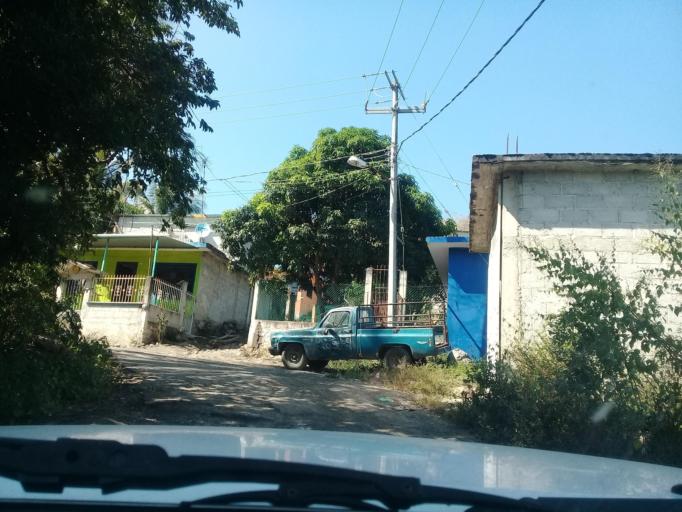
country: MX
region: Veracruz
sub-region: Emiliano Zapata
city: Plan del Rio
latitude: 19.4289
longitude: -96.6121
